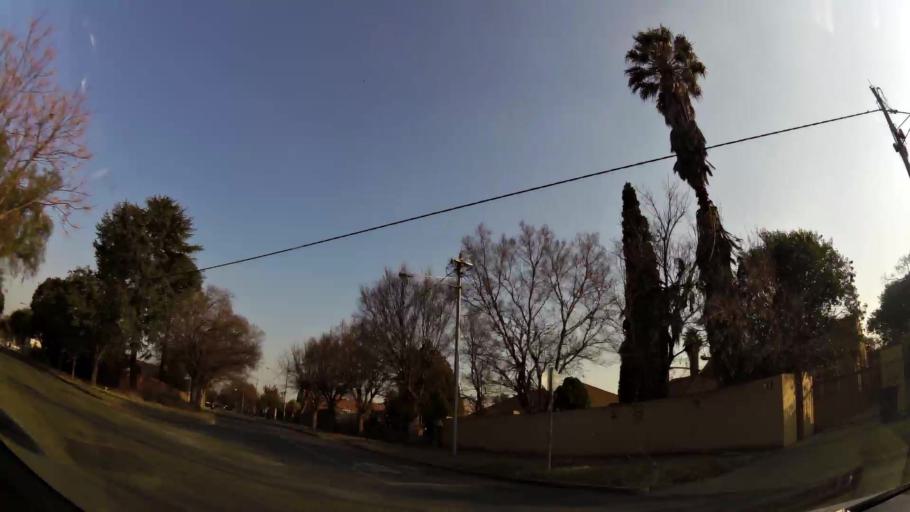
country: ZA
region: Gauteng
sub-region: Ekurhuleni Metropolitan Municipality
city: Springs
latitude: -26.2958
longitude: 28.4471
